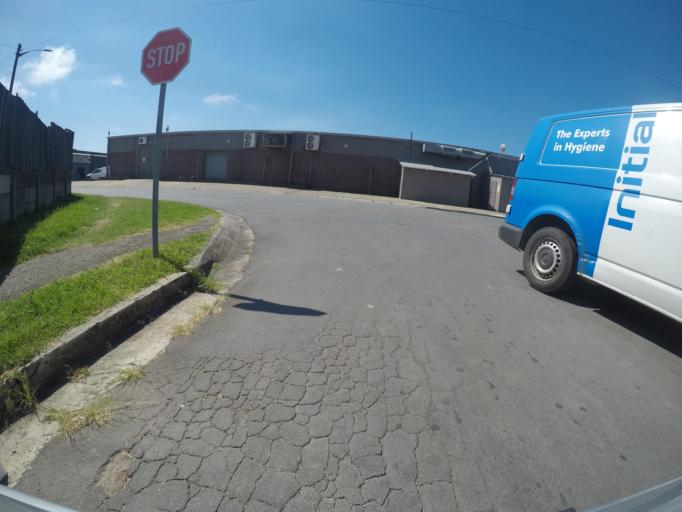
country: ZA
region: Eastern Cape
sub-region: Buffalo City Metropolitan Municipality
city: East London
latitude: -32.9756
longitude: 27.8925
